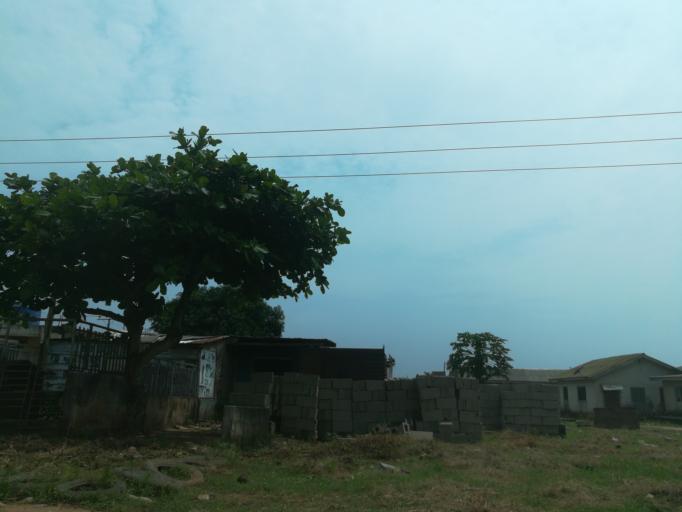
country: NG
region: Lagos
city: Ikorodu
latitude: 6.6051
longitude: 3.6000
